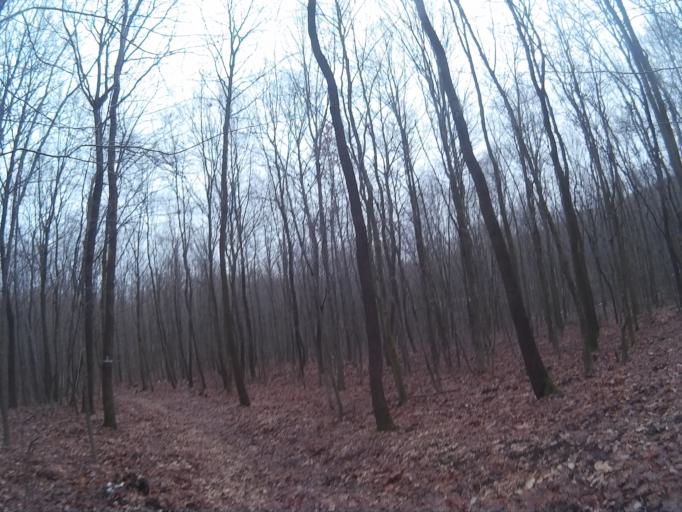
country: HU
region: Komarom-Esztergom
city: Tarjan
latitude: 47.6536
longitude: 18.4915
